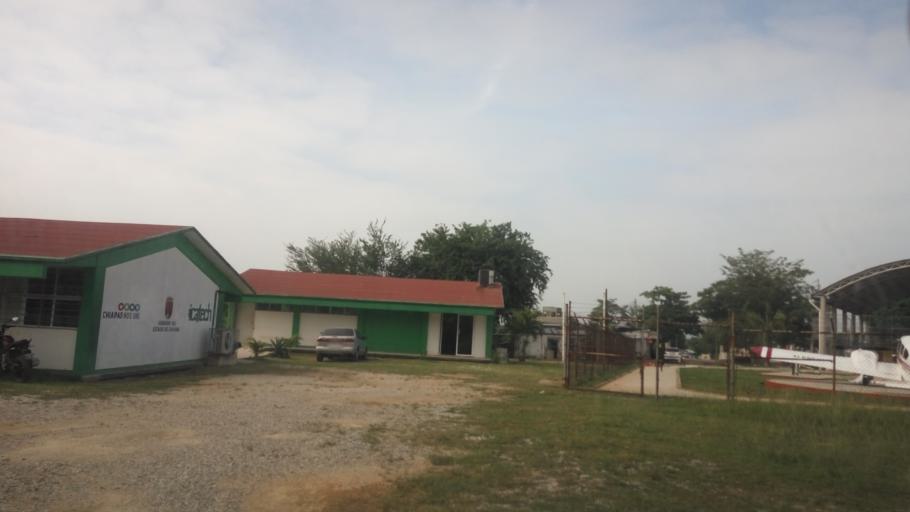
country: MX
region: Chiapas
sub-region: Reforma
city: El Carmen (El Limon)
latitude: 17.8592
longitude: -93.1506
